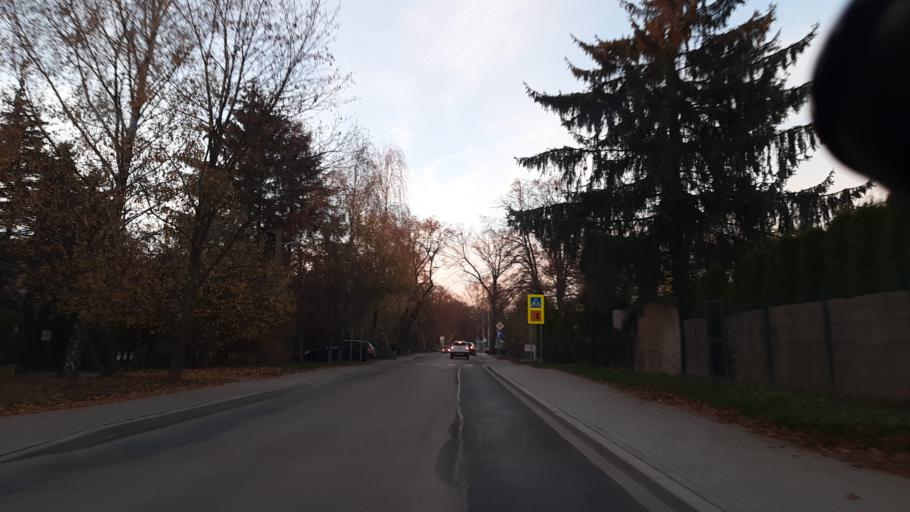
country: PL
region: Lublin Voivodeship
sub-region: Powiat lubelski
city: Lublin
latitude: 51.2747
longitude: 22.5087
